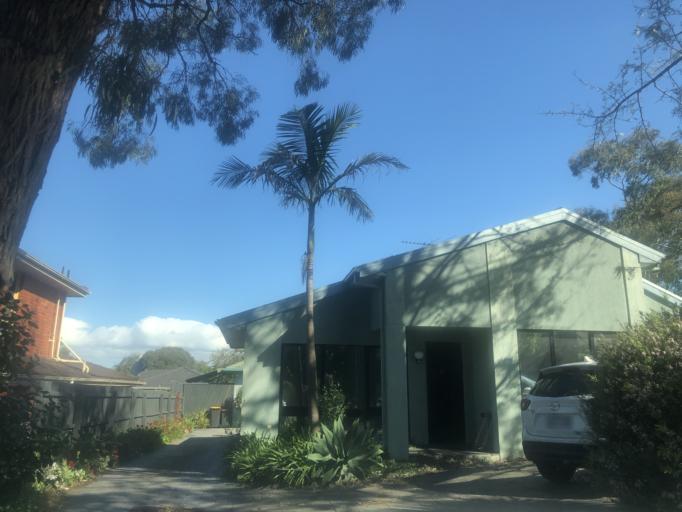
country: AU
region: Victoria
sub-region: Monash
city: Mulgrave
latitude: -37.9089
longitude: 145.1980
